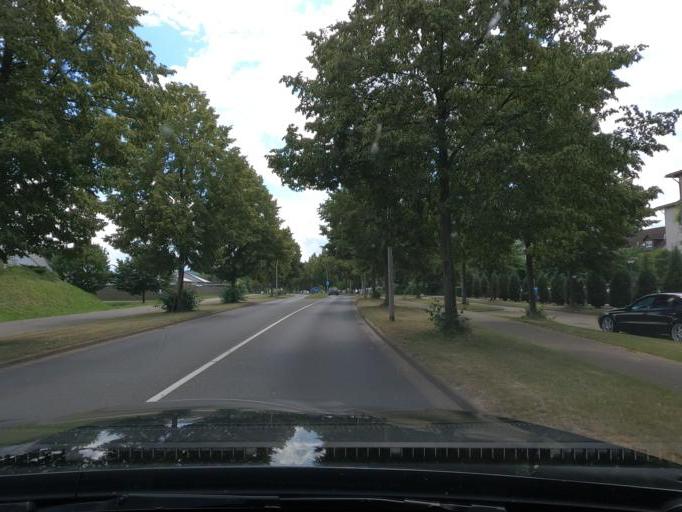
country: DE
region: Lower Saxony
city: Lengede
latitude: 52.1466
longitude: 10.2948
